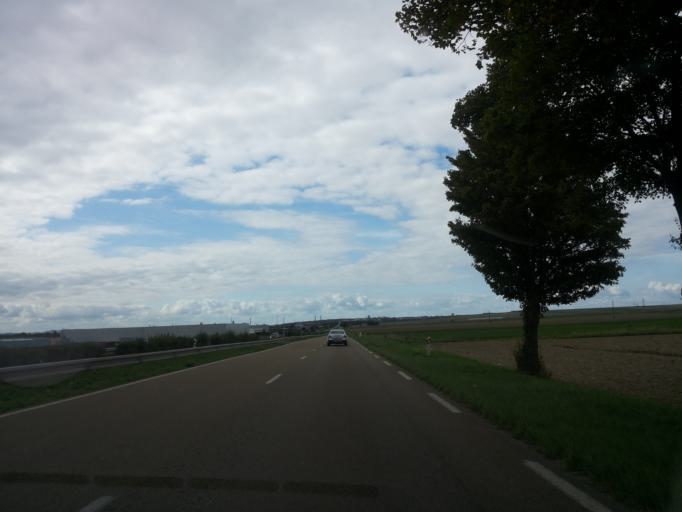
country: FR
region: Champagne-Ardenne
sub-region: Departement de la Marne
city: Sillery
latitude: 49.2196
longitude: 4.1257
